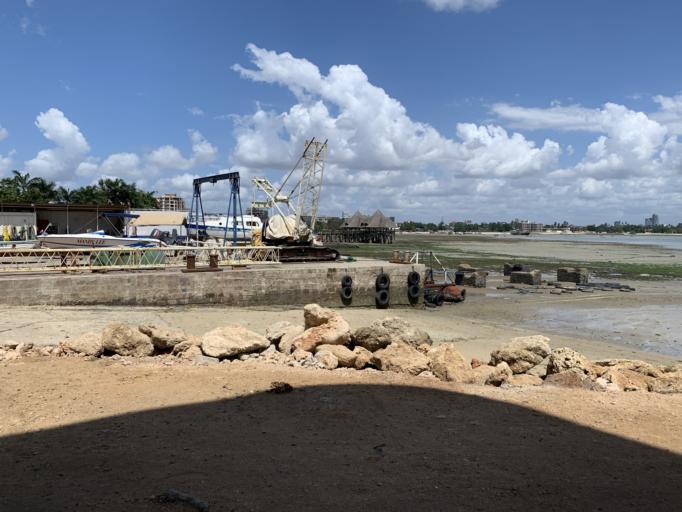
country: TZ
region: Dar es Salaam
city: Magomeni
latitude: -6.7529
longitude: 39.2723
